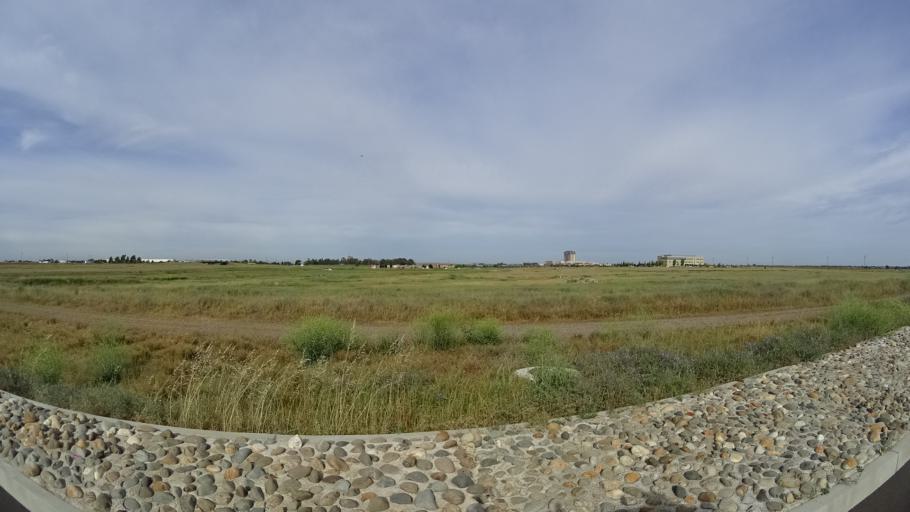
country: US
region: California
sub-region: Placer County
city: Lincoln
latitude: 38.8351
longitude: -121.2925
